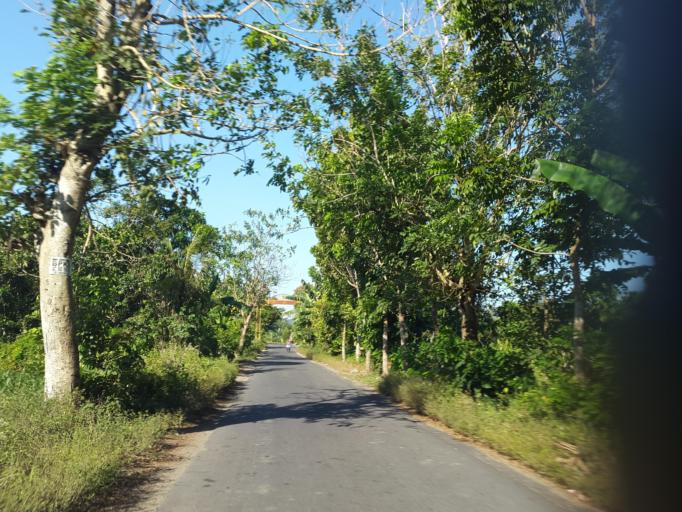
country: ID
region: West Nusa Tenggara
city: Karangkebon Timur
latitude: -8.6892
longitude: 116.1112
